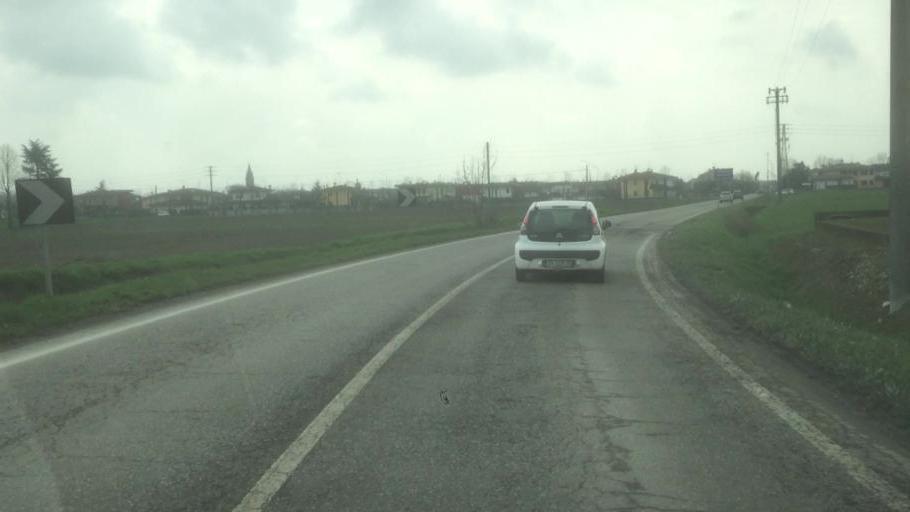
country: IT
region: Lombardy
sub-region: Provincia di Mantova
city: Casaloldo
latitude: 45.2612
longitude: 10.4772
